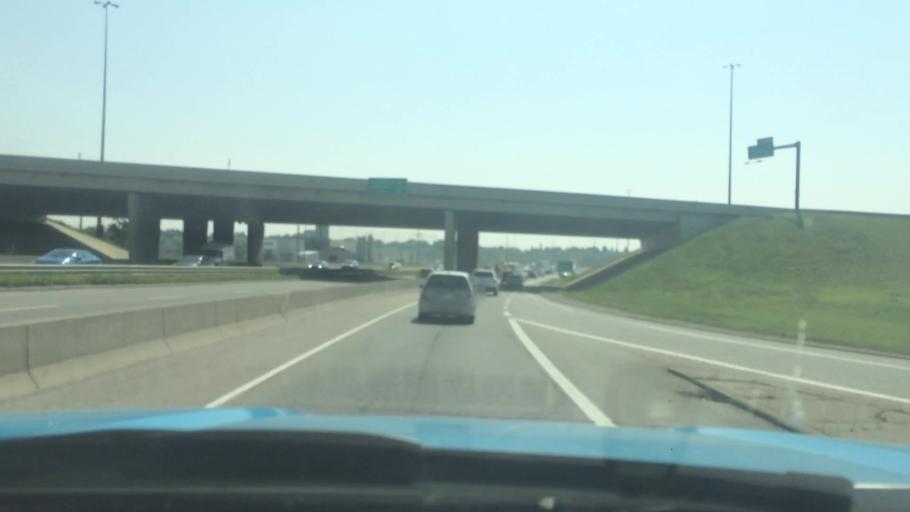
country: CA
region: Alberta
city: Calgary
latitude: 50.9934
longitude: -114.0362
